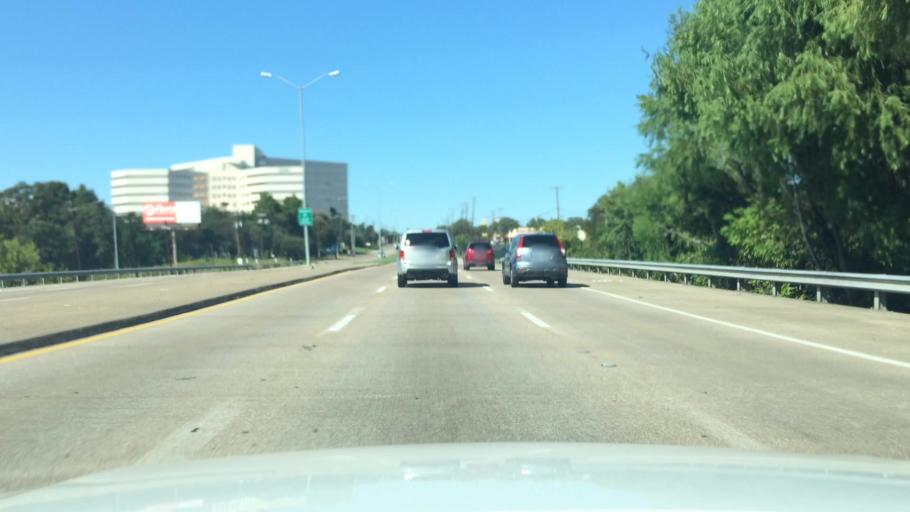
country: US
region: Texas
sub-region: Dallas County
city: Addison
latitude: 32.9455
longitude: -96.8035
